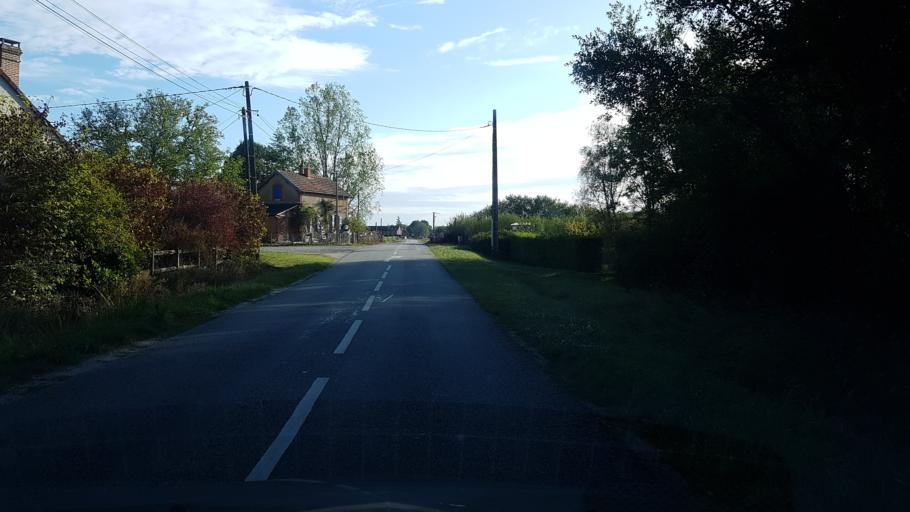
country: FR
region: Centre
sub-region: Departement du Loiret
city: Cerdon
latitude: 47.6913
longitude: 2.3596
